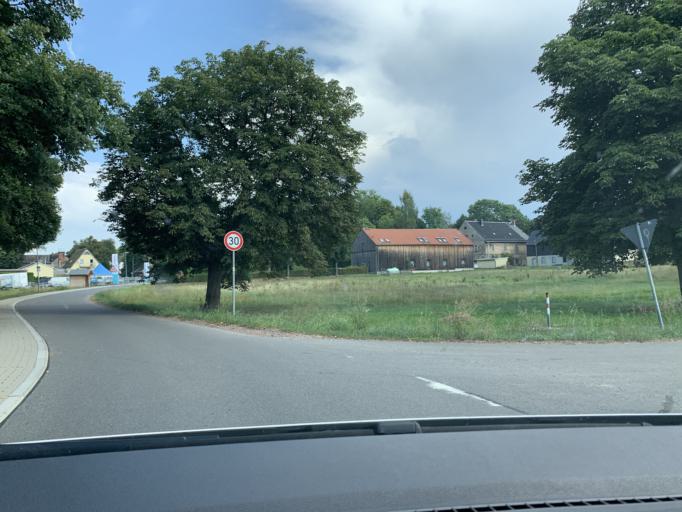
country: DE
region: Saxony
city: Frankenberg
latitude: 50.9238
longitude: 13.0717
